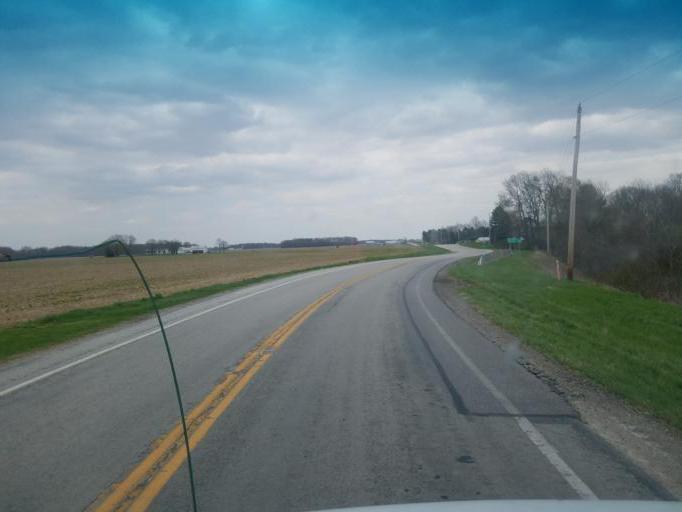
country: US
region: Ohio
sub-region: Seneca County
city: Tiffin
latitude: 40.9500
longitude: -83.1363
